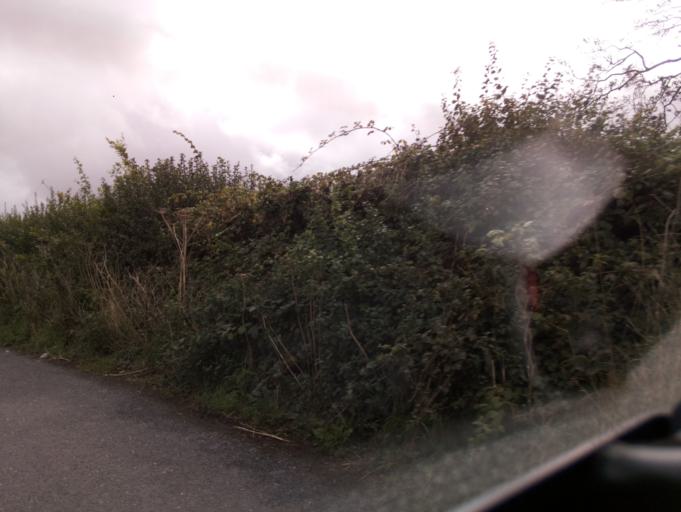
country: GB
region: England
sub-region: Devon
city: Kingsbridge
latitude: 50.2715
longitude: -3.7132
